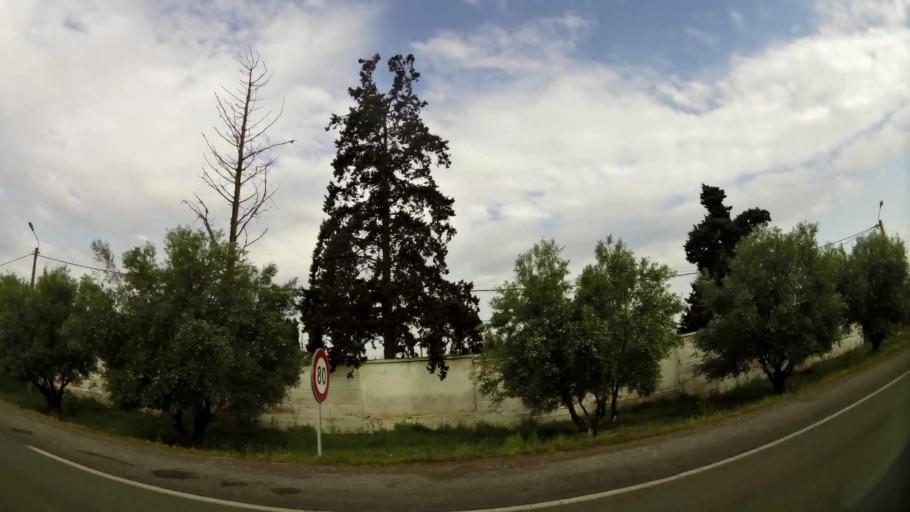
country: MA
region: Rabat-Sale-Zemmour-Zaer
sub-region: Khemisset
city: Khemisset
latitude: 33.8004
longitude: -6.0973
